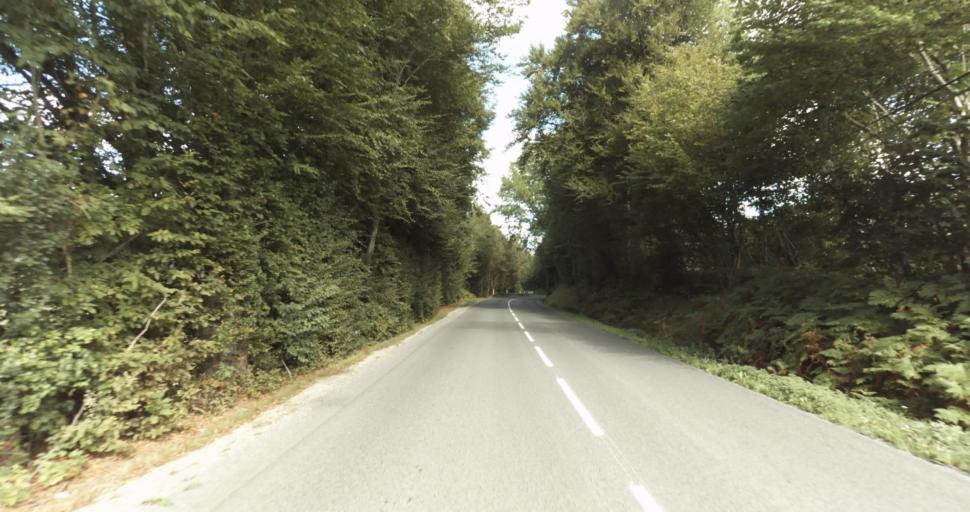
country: FR
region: Lower Normandy
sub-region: Departement de l'Orne
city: Vimoutiers
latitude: 48.9095
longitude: 0.2560
